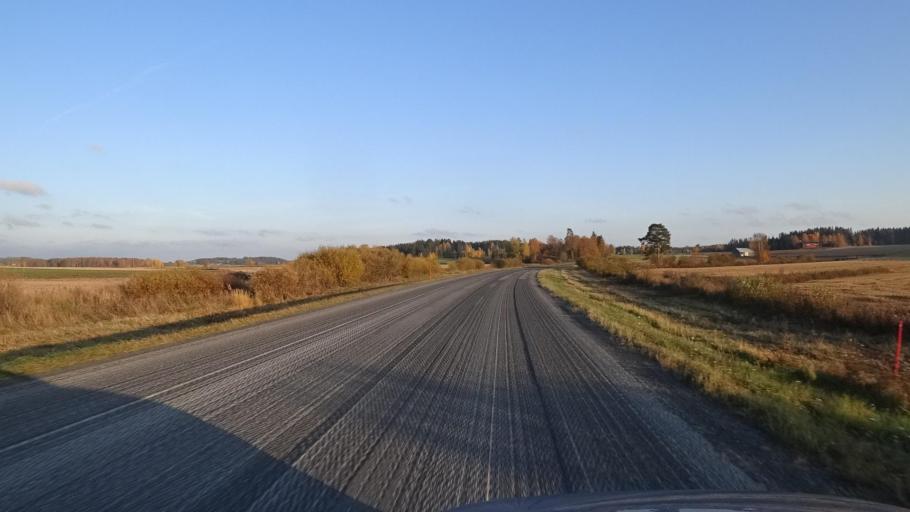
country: FI
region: Haeme
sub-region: Forssa
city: Ypaejae
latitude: 60.7855
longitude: 23.3010
